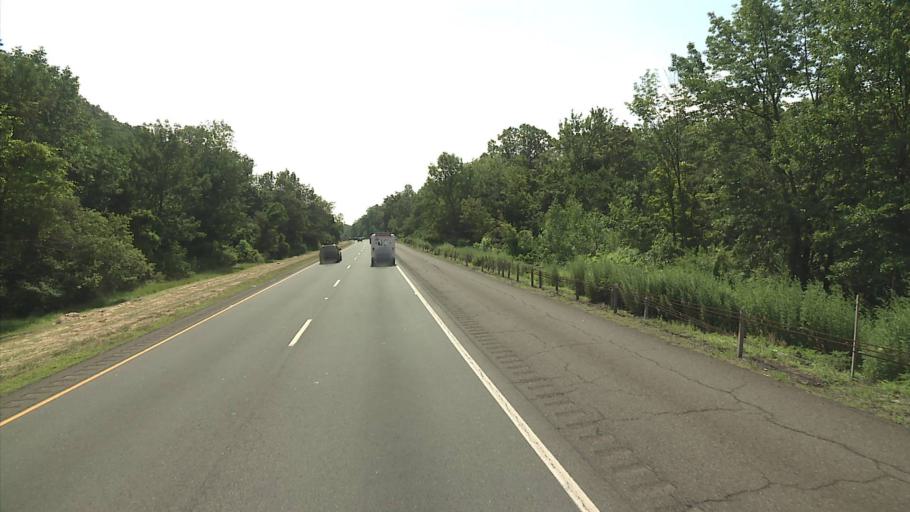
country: US
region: Connecticut
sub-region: New Haven County
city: Meriden
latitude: 41.5524
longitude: -72.8384
